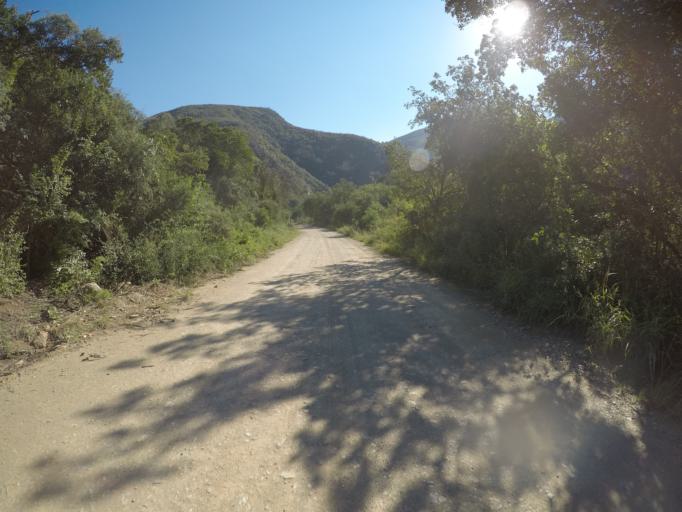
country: ZA
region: Eastern Cape
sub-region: Cacadu District Municipality
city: Kareedouw
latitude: -33.6617
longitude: 24.5407
